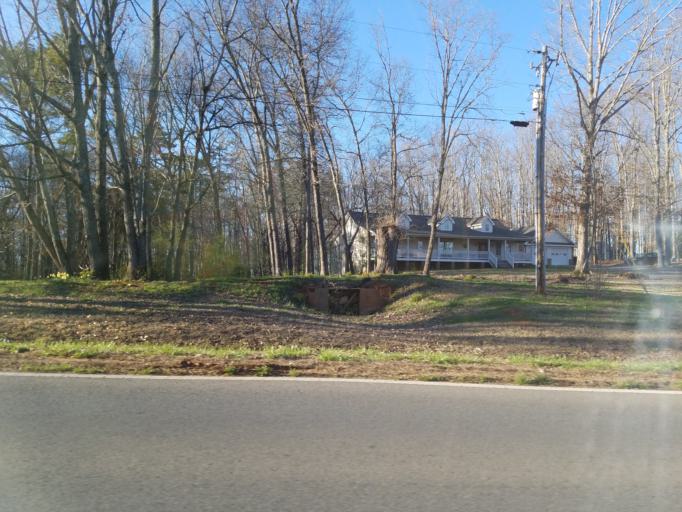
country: US
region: Georgia
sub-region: Pickens County
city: Jasper
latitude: 34.4367
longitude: -84.4253
